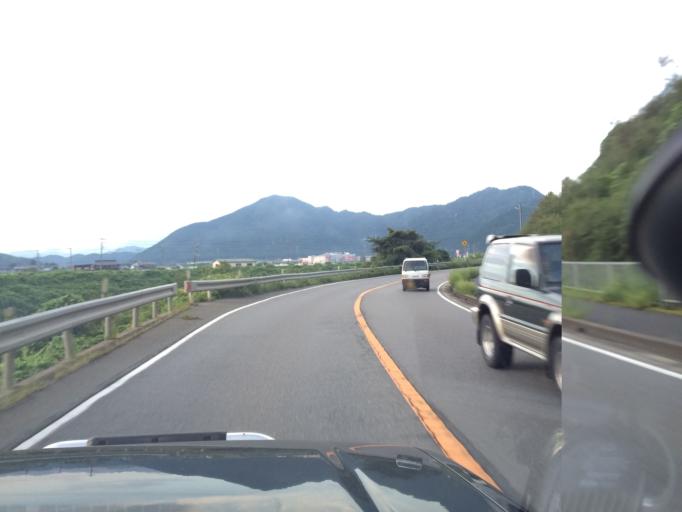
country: JP
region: Kyoto
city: Fukuchiyama
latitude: 35.1520
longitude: 135.0399
